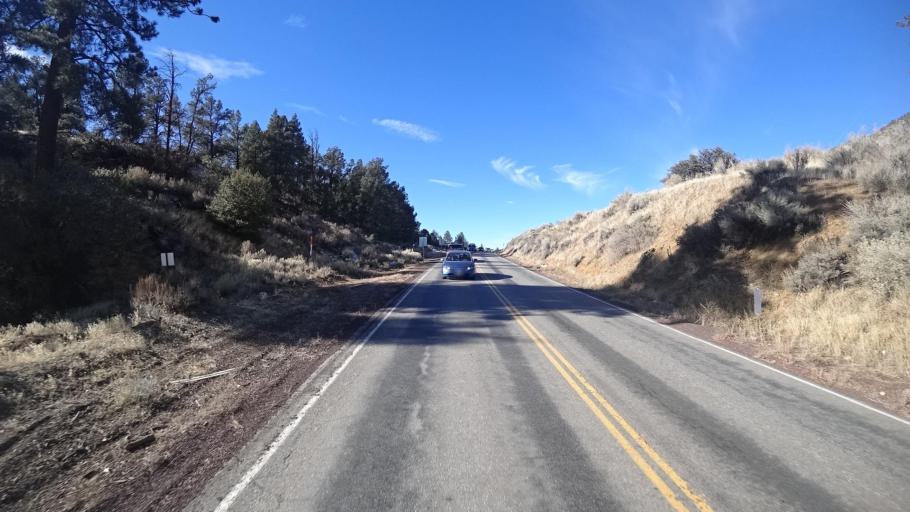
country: US
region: California
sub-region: Kern County
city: Frazier Park
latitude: 34.8257
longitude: -119.0148
